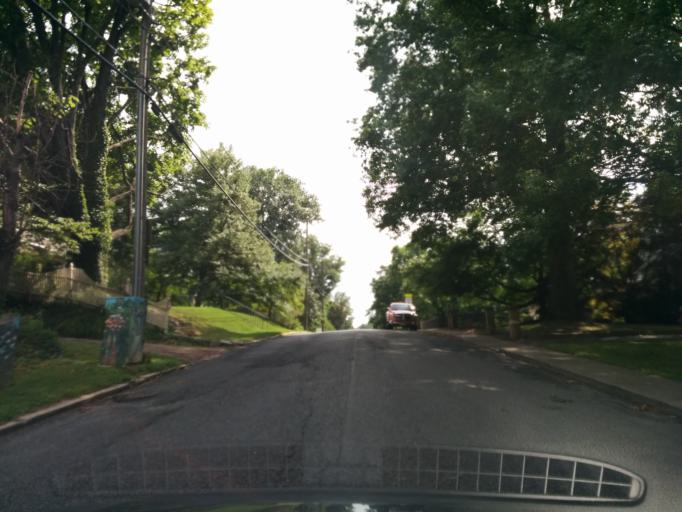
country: US
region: Virginia
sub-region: City of Lexington
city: Lexington
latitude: 37.7822
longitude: -79.4491
